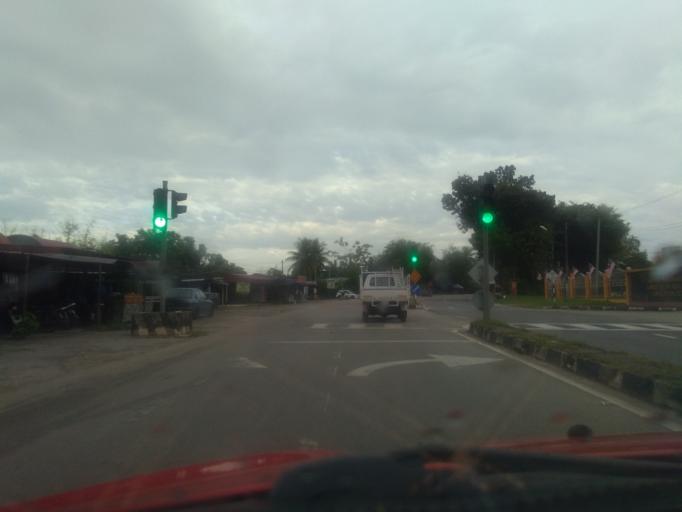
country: MY
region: Kedah
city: Sungai Petani
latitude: 5.6304
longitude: 100.5231
